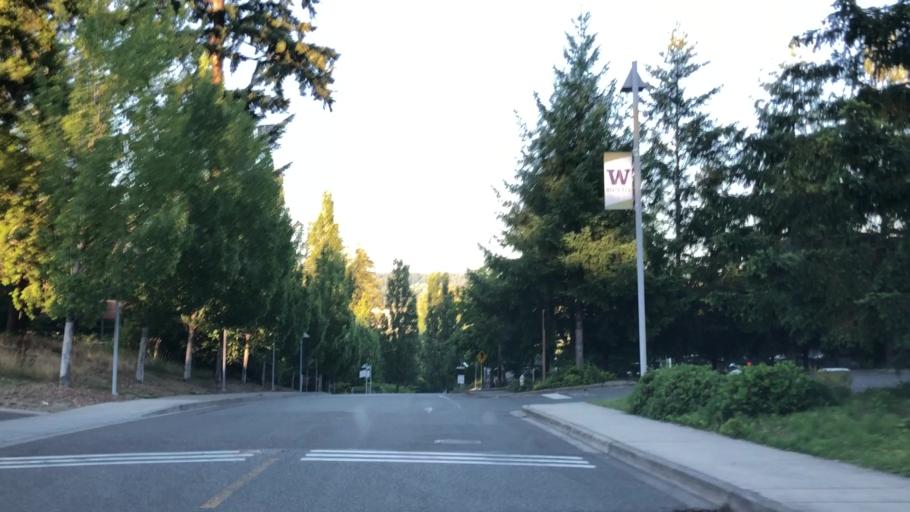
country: US
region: Washington
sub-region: King County
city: Bothell
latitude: 47.7583
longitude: -122.1927
